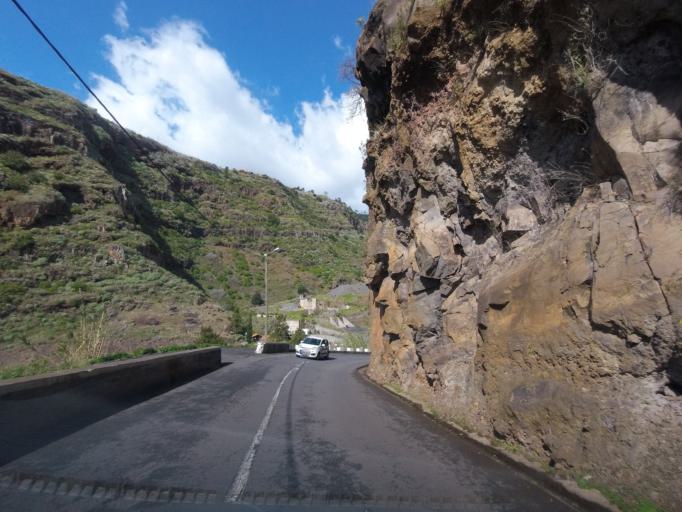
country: PT
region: Madeira
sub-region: Calheta
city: Estreito da Calheta
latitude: 32.7359
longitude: -17.1995
